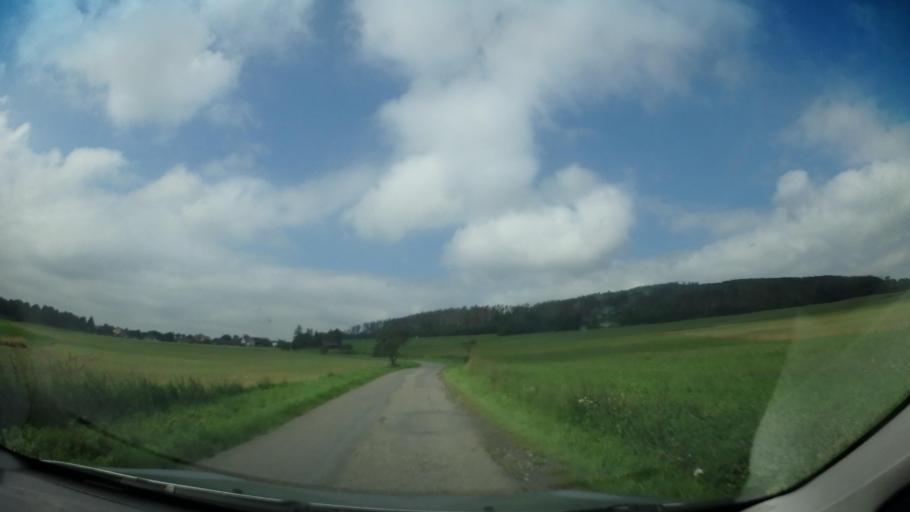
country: CZ
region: Central Bohemia
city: Sedlcany
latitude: 49.7035
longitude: 14.3610
